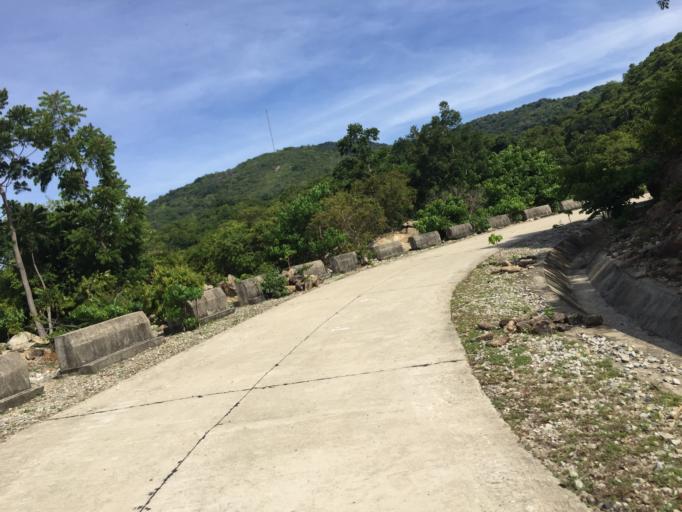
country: VN
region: Quang Nam
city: Hoi An
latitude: 15.9328
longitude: 108.5308
